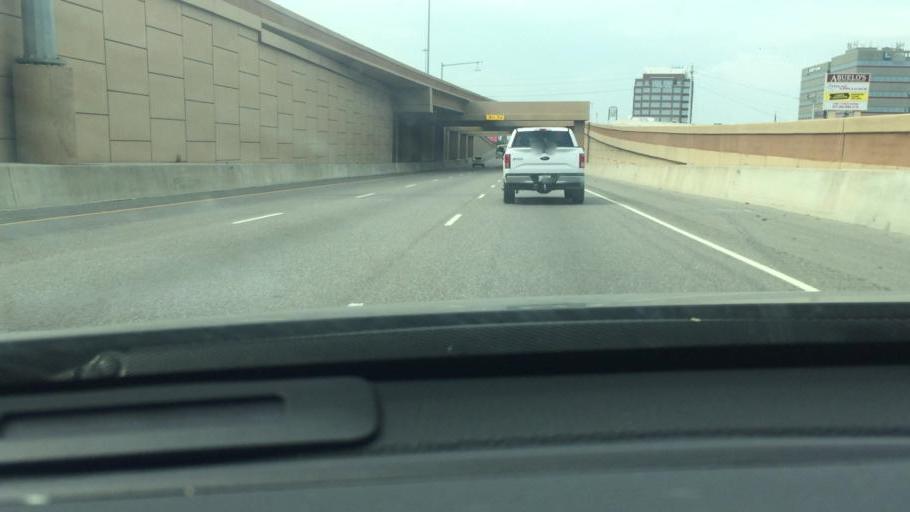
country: US
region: Texas
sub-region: Tarrant County
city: Hurst
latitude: 32.8394
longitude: -97.1874
